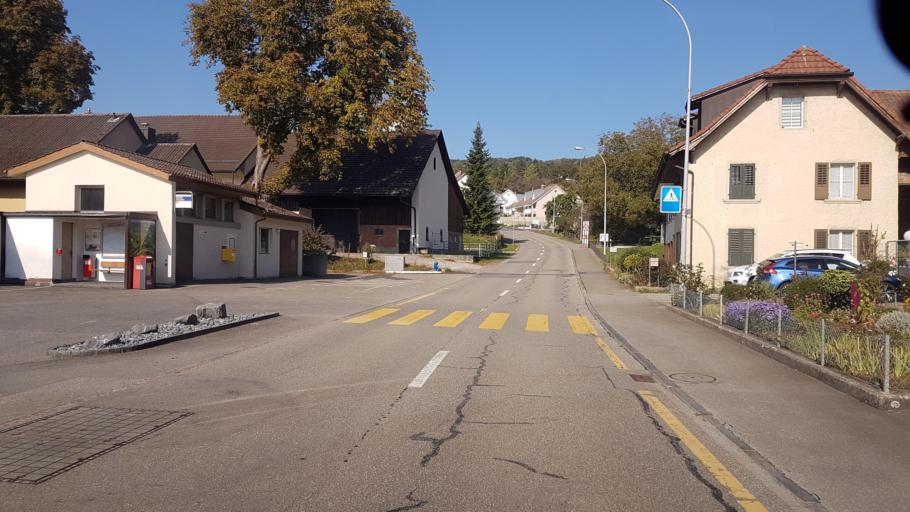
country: CH
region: Aargau
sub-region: Bezirk Brugg
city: Villnachern
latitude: 47.5170
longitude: 8.1446
